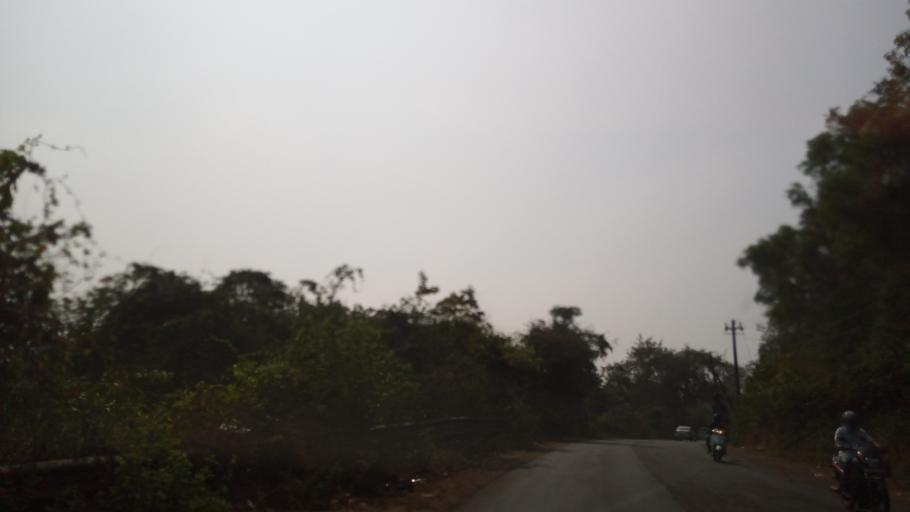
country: IN
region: Goa
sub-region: North Goa
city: Serula
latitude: 15.5423
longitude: 73.8163
